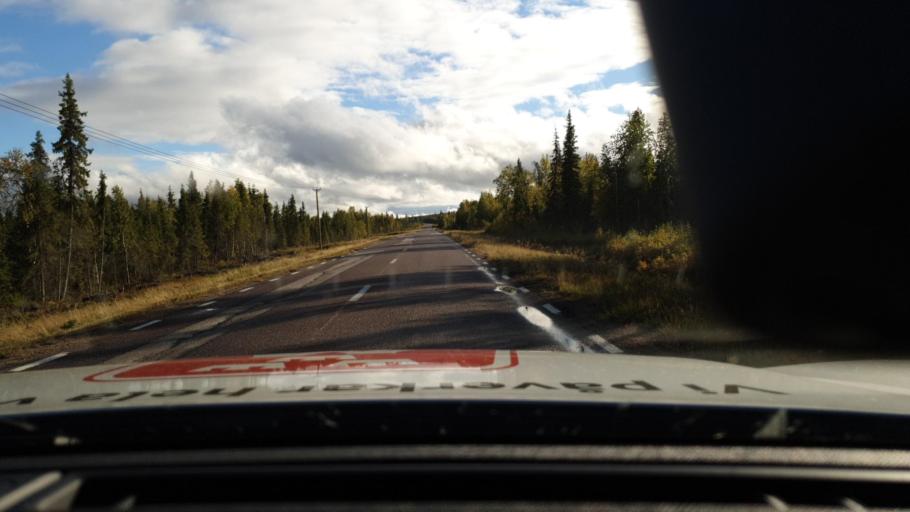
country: SE
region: Norrbotten
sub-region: Overkalix Kommun
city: OEverkalix
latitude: 66.8755
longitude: 22.7612
